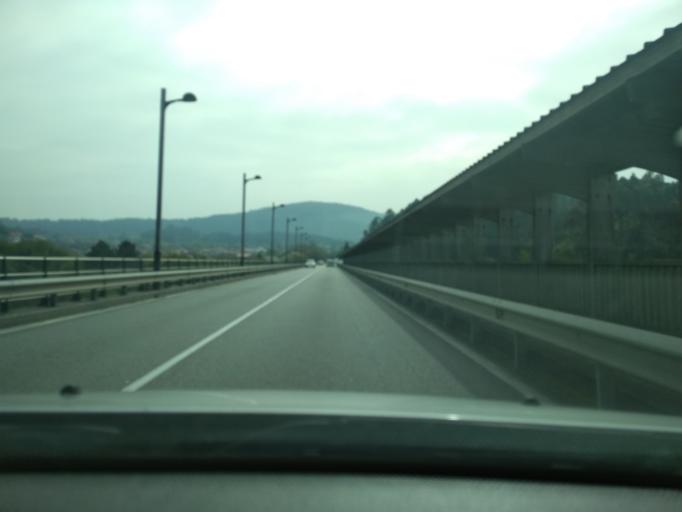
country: ES
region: Galicia
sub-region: Provincia de Pontevedra
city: Catoira
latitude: 42.6767
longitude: -8.7219
